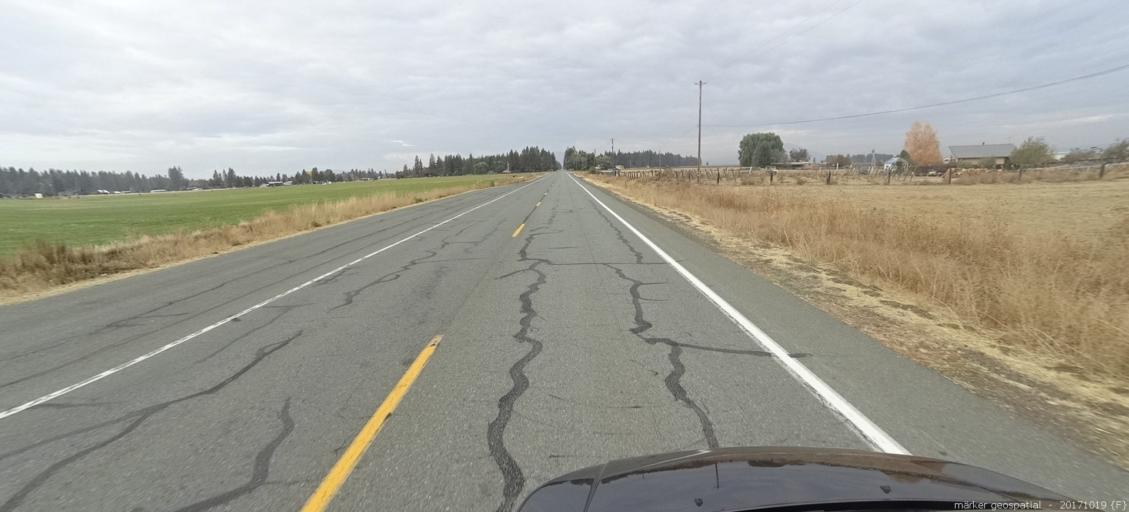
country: US
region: California
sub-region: Shasta County
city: Burney
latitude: 41.0755
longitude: -121.3235
